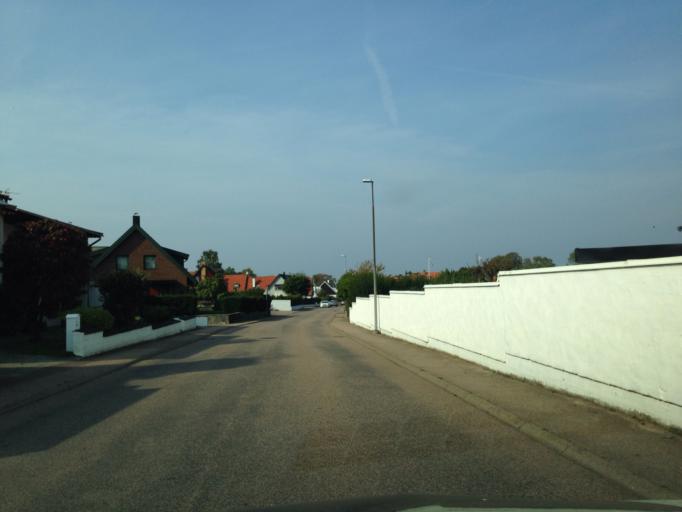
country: SE
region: Skane
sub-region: Bastads Kommun
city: Bastad
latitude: 56.4289
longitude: 12.8462
